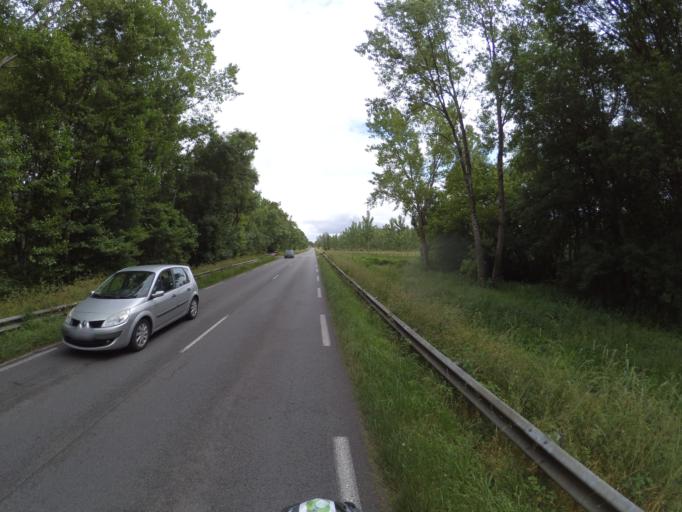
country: FR
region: Aquitaine
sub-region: Departement de la Gironde
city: Soussans
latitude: 45.0647
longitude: -0.7198
